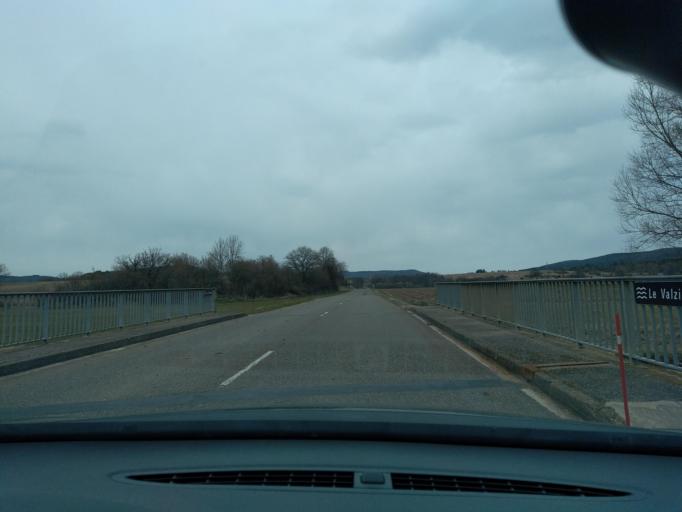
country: FR
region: Franche-Comte
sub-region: Departement du Jura
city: Arinthod
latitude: 46.4221
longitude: 5.5550
